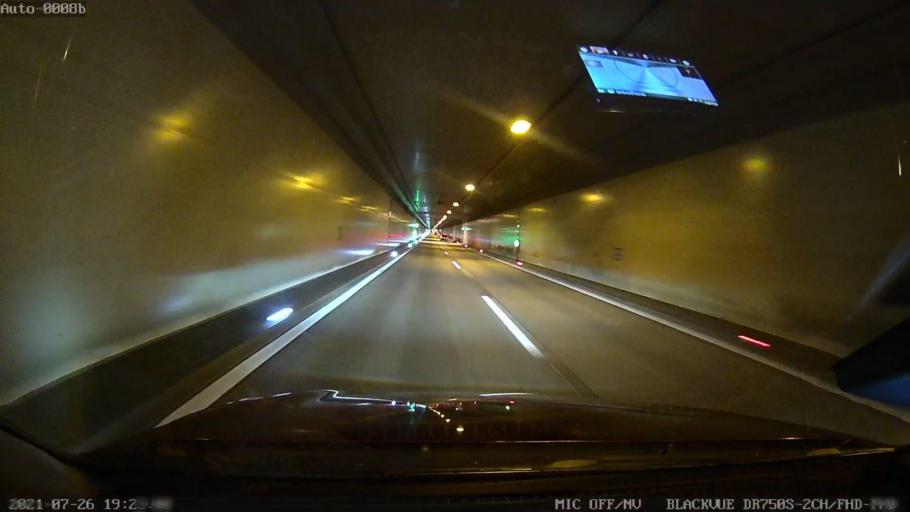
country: AT
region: Upper Austria
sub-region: Politischer Bezirk Kirchdorf an der Krems
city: Micheldorf in Oberoesterreich
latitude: 47.8820
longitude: 14.1105
